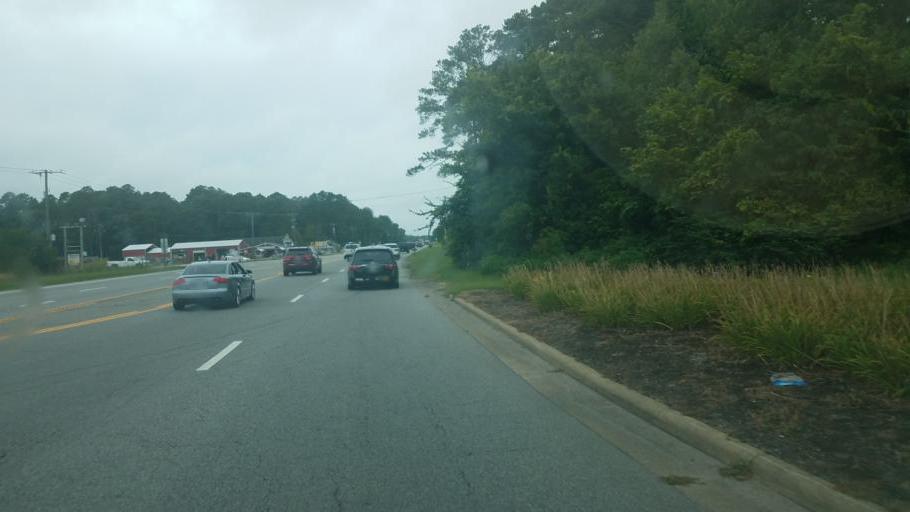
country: US
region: North Carolina
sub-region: Currituck County
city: Currituck
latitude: 36.4527
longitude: -76.0760
